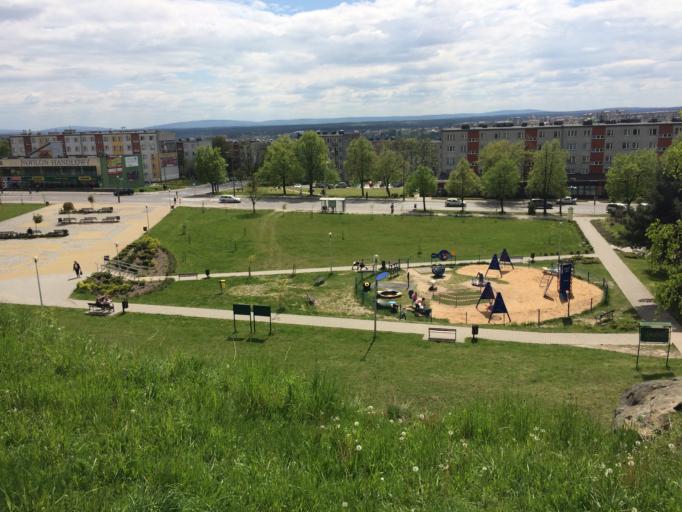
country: PL
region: Swietokrzyskie
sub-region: Powiat starachowicki
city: Starachowice
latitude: 51.0505
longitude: 21.0803
